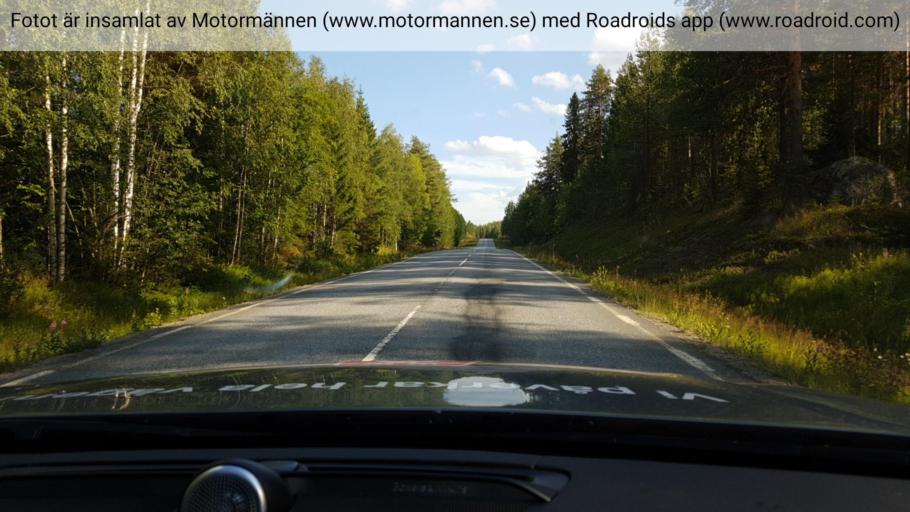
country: SE
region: Vaesterbotten
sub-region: Dorotea Kommun
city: Dorotea
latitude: 63.8955
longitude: 16.3617
